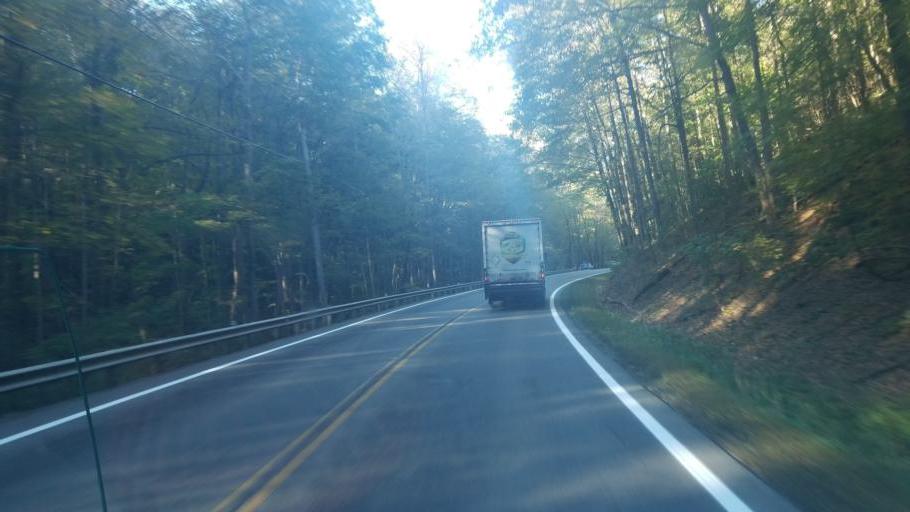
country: US
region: Ohio
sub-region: Columbiana County
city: Glenmoor
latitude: 40.7407
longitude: -80.6397
